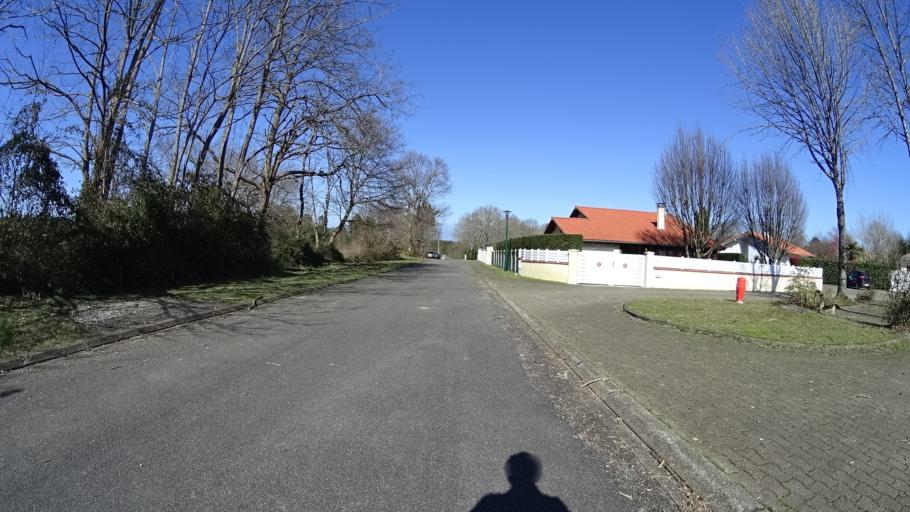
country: FR
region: Aquitaine
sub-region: Departement des Landes
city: Saint-Paul-les-Dax
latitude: 43.7339
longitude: -1.0844
